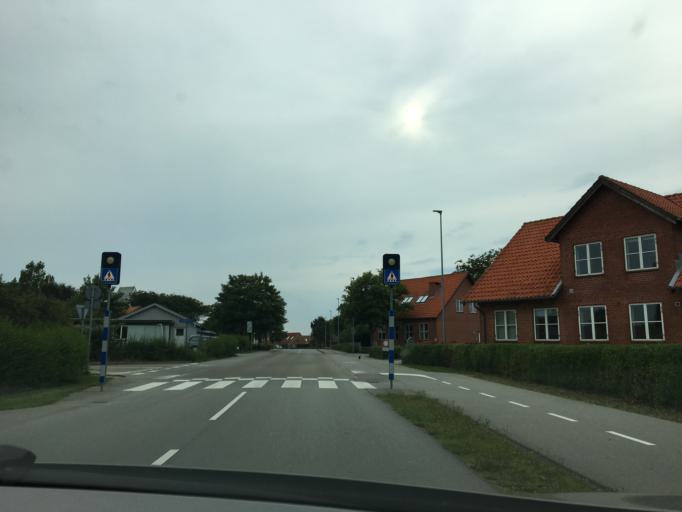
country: DK
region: Central Jutland
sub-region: Ringkobing-Skjern Kommune
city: Ringkobing
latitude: 56.0945
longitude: 8.2687
